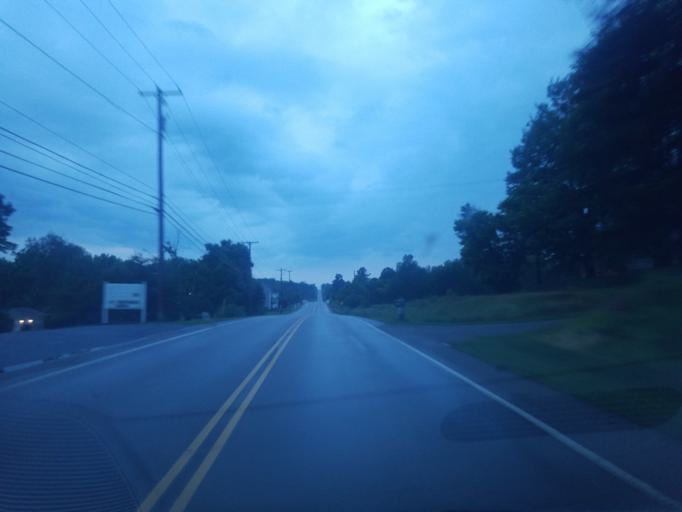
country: US
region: Ohio
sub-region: Mahoning County
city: Canfield
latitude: 40.9881
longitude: -80.7202
